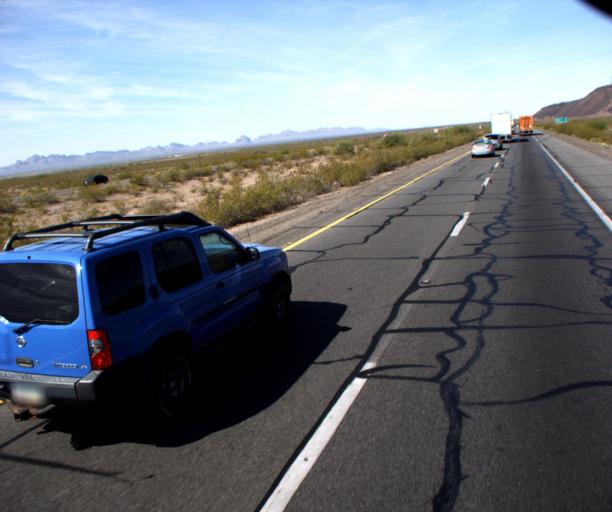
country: US
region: Arizona
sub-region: Maricopa County
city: Buckeye
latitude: 33.5227
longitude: -113.0803
